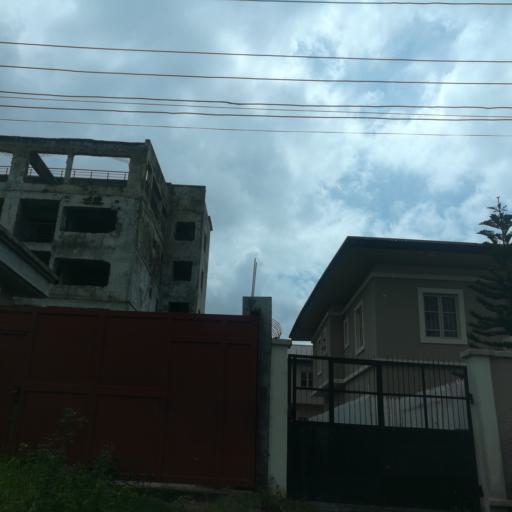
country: NG
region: Lagos
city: Ikoyi
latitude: 6.4411
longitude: 3.4624
